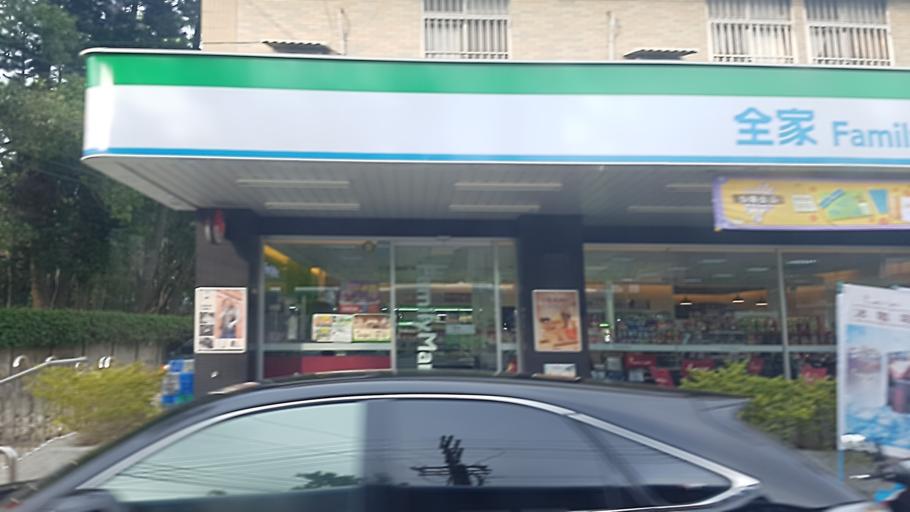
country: TW
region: Taiwan
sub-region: Hsinchu
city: Hsinchu
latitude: 24.7765
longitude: 120.9430
